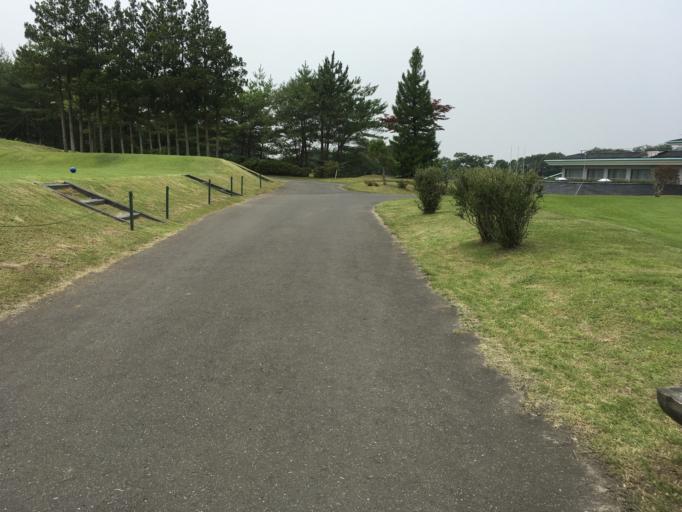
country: JP
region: Iwate
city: Ichinoseki
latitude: 38.8801
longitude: 141.0761
